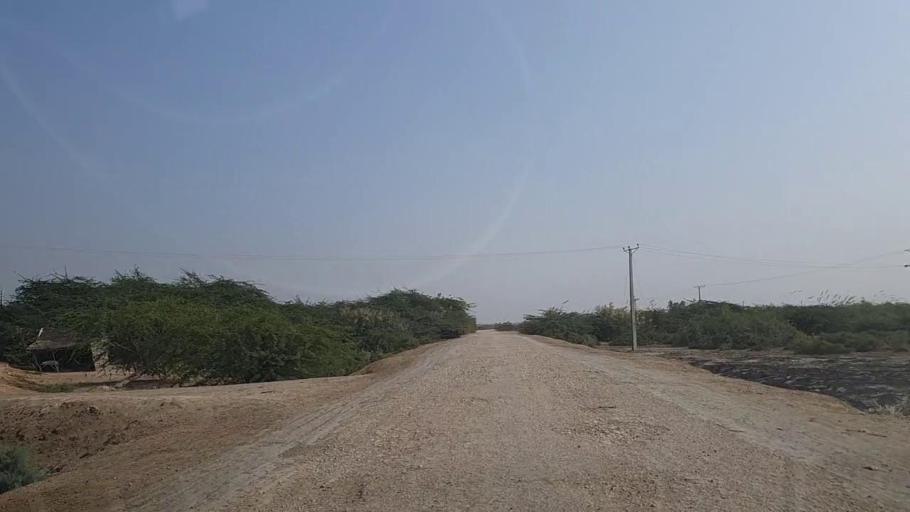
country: PK
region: Sindh
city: Keti Bandar
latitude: 24.2547
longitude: 67.6225
